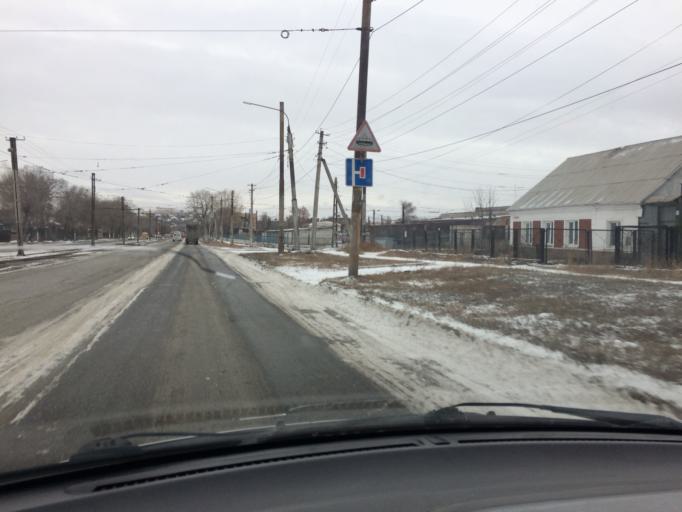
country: RU
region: Chelyabinsk
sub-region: Gorod Magnitogorsk
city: Magnitogorsk
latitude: 53.3862
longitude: 59.0790
